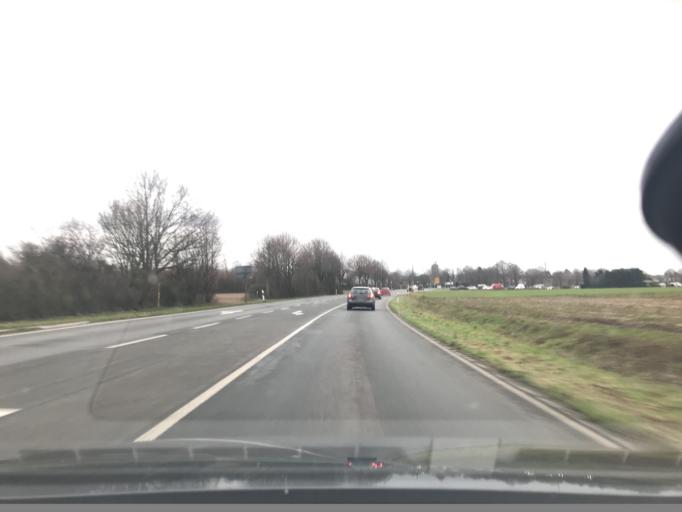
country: DE
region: North Rhine-Westphalia
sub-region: Regierungsbezirk Dusseldorf
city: Uedem
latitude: 51.6762
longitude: 6.2696
